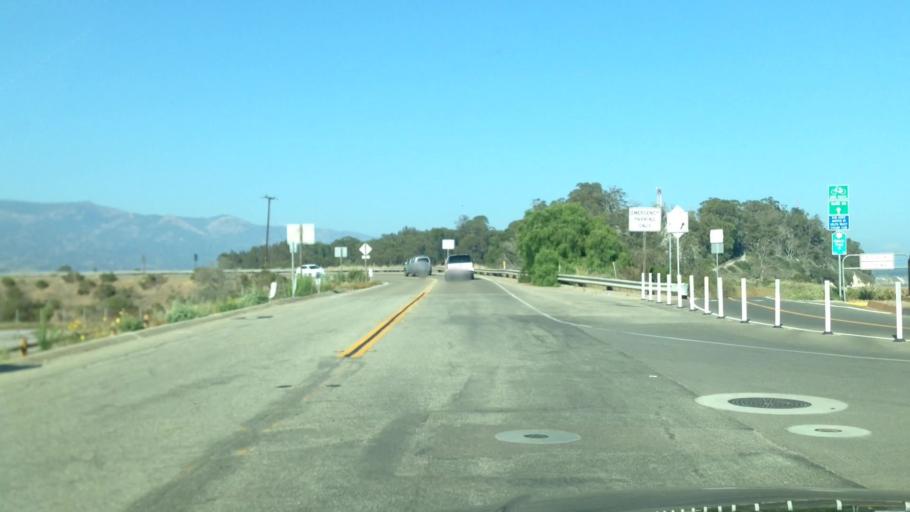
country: US
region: California
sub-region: Santa Barbara County
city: Goleta
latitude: 34.4181
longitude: -119.8318
